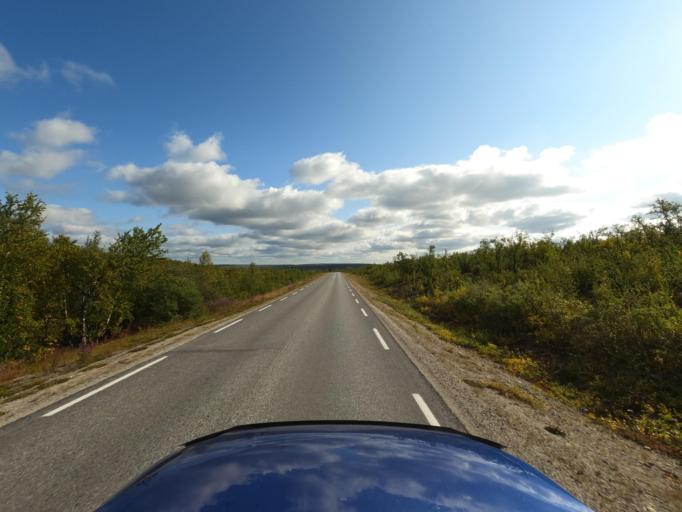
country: NO
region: Finnmark Fylke
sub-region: Porsanger
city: Lakselv
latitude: 69.3938
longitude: 24.5721
